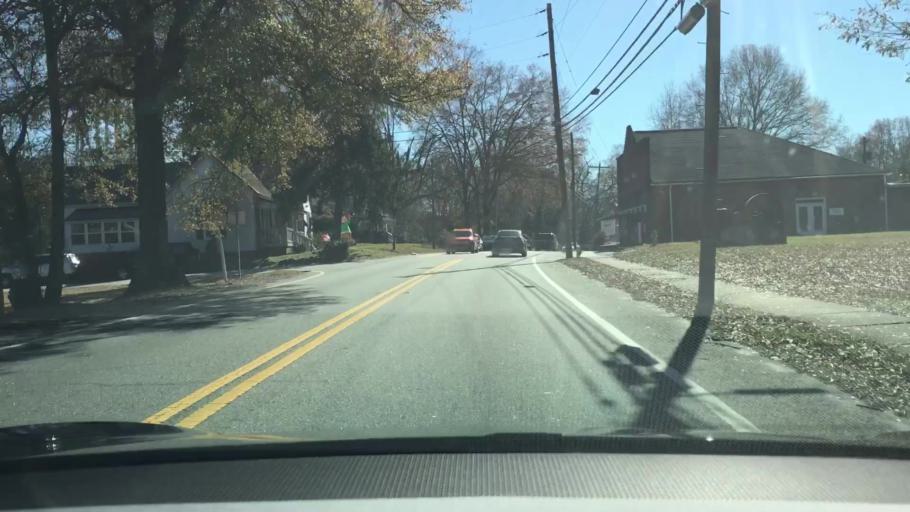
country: US
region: Georgia
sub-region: Walton County
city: Monroe
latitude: 33.7856
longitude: -83.7090
